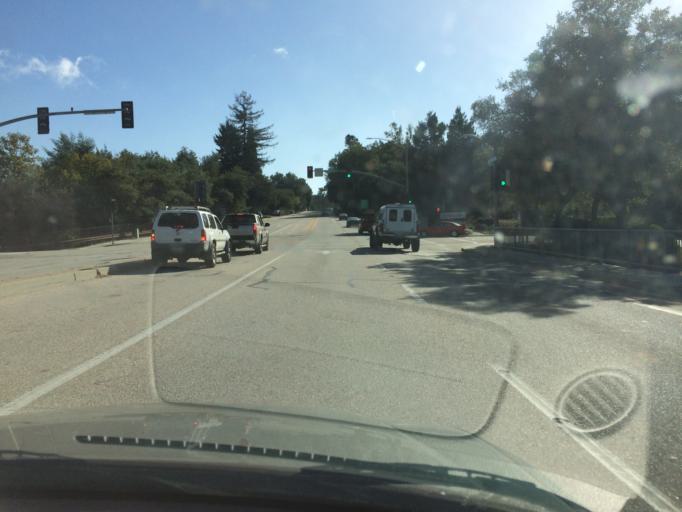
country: US
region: California
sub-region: Santa Cruz County
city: Scotts Valley
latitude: 37.0414
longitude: -122.0243
